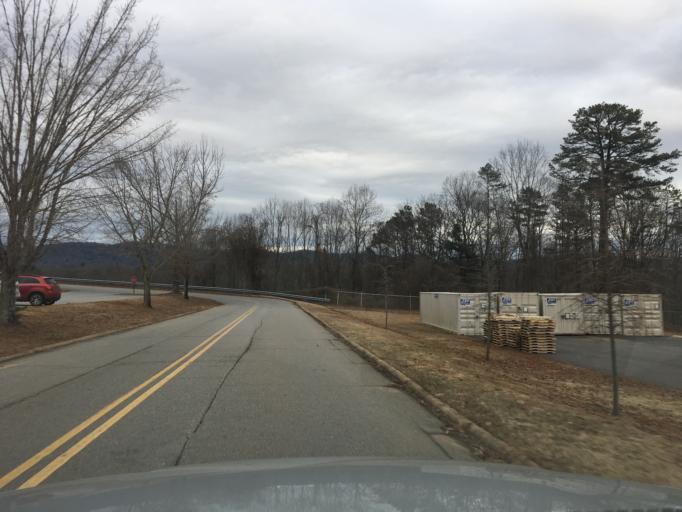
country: US
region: North Carolina
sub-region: Buncombe County
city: Woodfin
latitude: 35.6054
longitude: -82.5838
